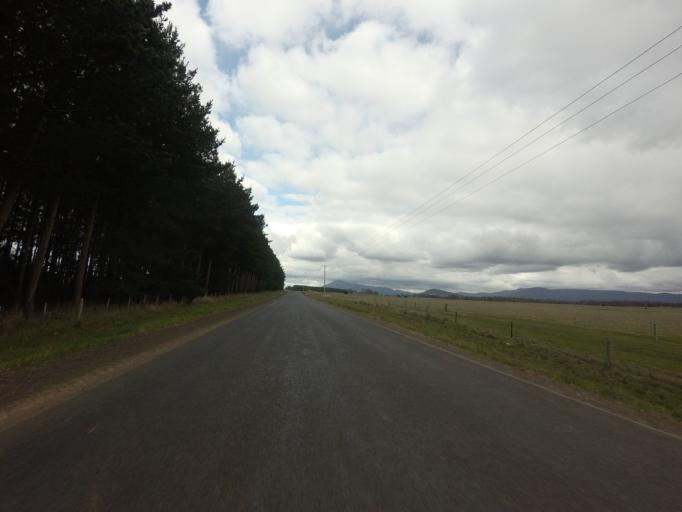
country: AU
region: Tasmania
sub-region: Northern Midlands
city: Longford
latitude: -41.7708
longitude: 147.0883
